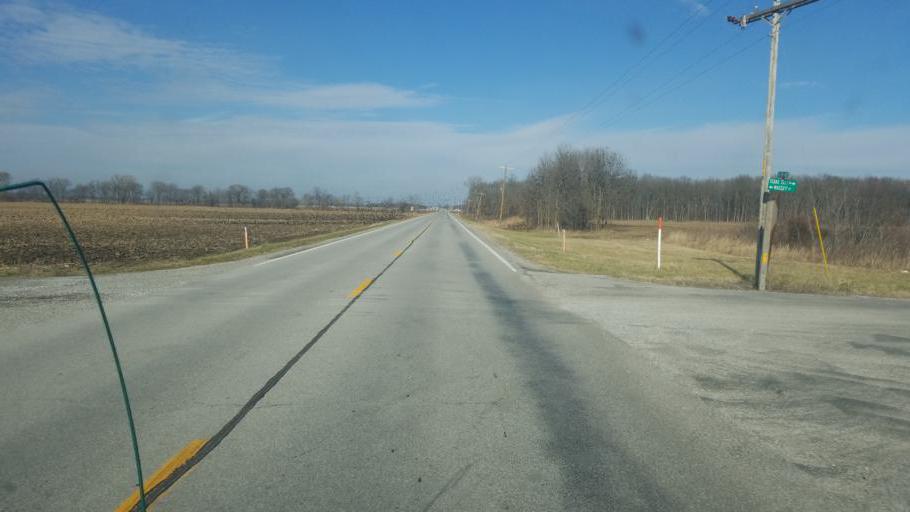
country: US
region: Illinois
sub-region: Saline County
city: Eldorado
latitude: 37.8778
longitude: -88.4530
